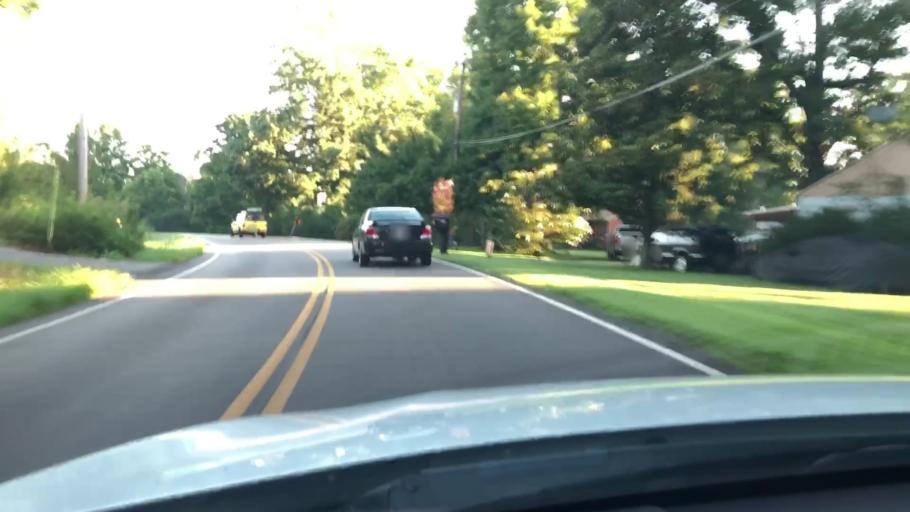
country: US
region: Kentucky
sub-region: Jefferson County
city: Middletown
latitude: 38.2202
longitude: -85.5081
